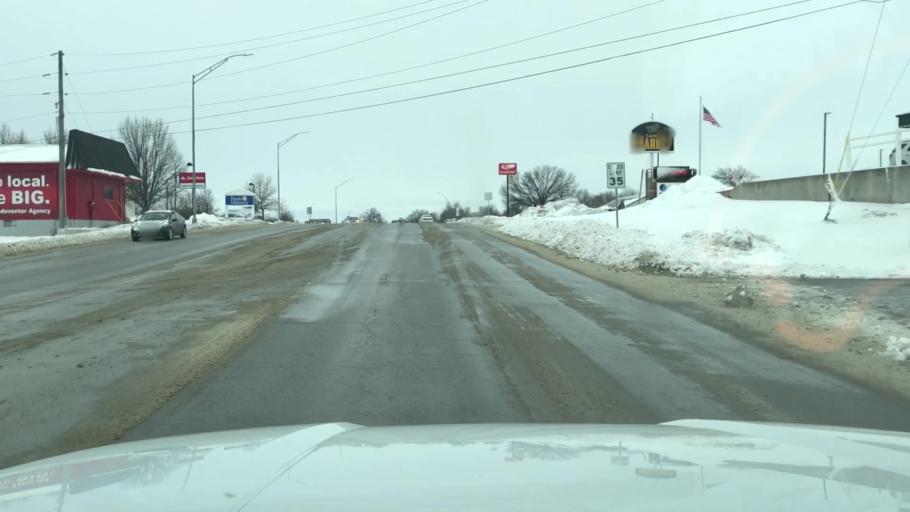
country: US
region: Missouri
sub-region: Clinton County
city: Cameron
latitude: 39.7509
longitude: -94.2346
